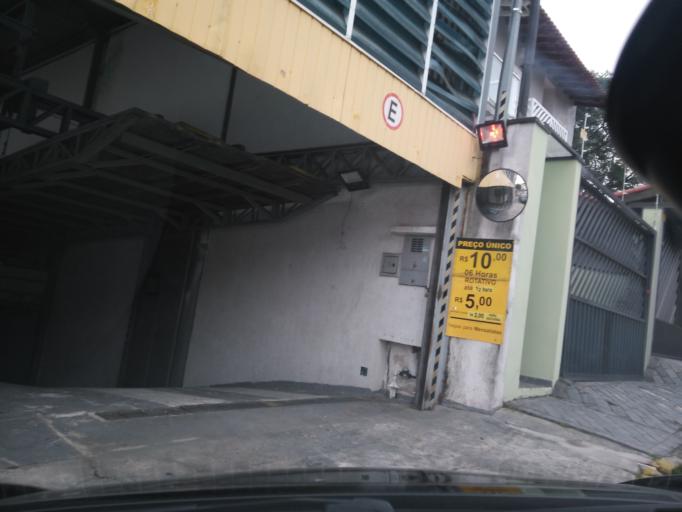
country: BR
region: Sao Paulo
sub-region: Sao Bernardo Do Campo
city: Sao Bernardo do Campo
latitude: -23.7156
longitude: -46.5564
